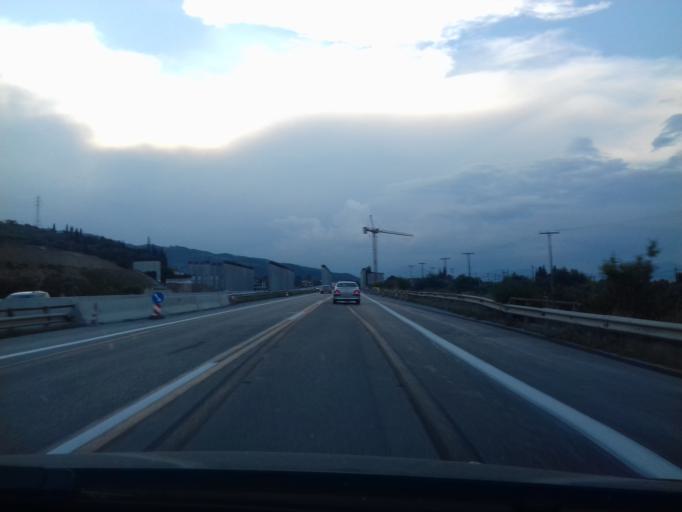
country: GR
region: West Greece
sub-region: Nomos Achaias
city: Selianitika
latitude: 38.2903
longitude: 22.0156
